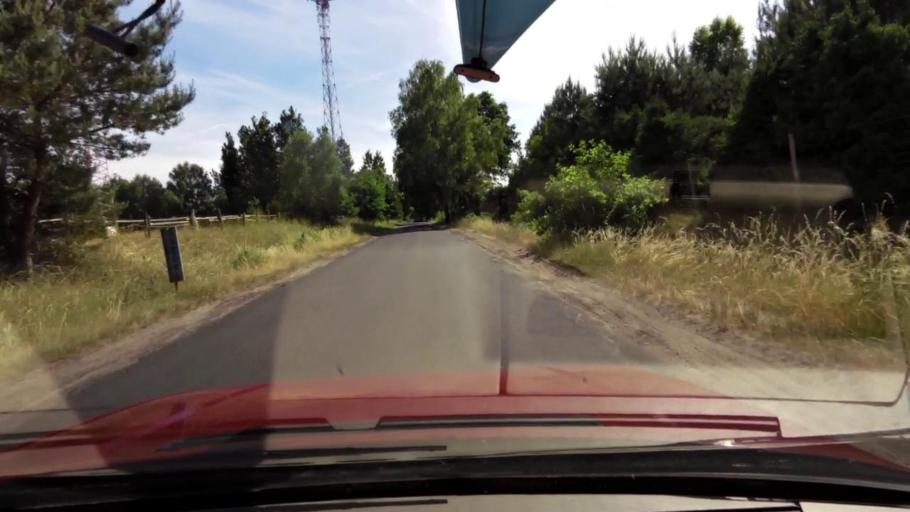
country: PL
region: Pomeranian Voivodeship
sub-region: Powiat slupski
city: Kepice
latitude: 54.2852
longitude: 16.9586
